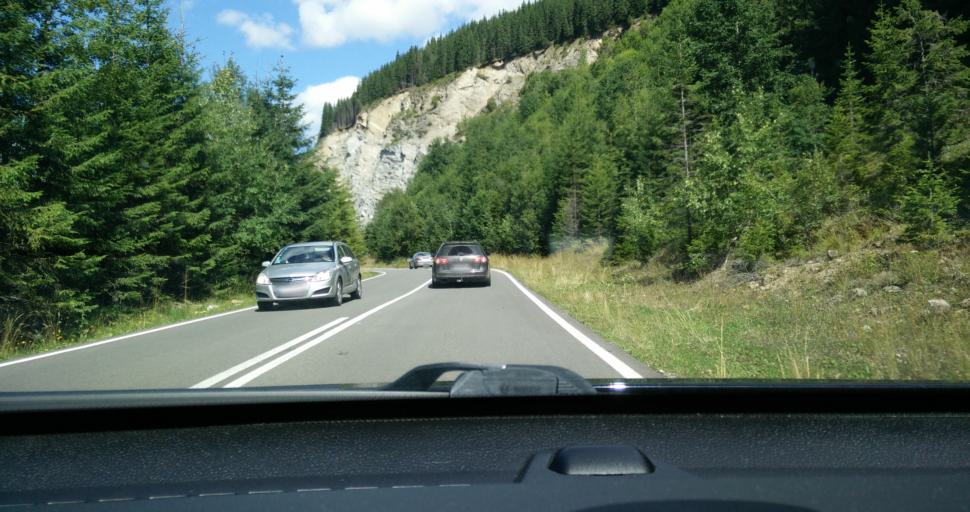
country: RO
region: Alba
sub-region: Comuna Sugag
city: Sugag
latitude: 45.5481
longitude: 23.6323
